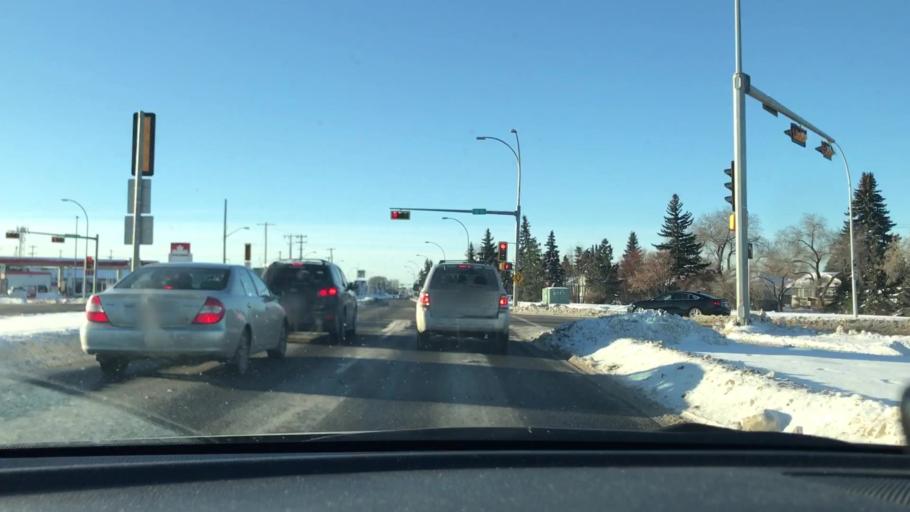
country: CA
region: Alberta
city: Edmonton
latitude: 53.5087
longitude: -113.4424
